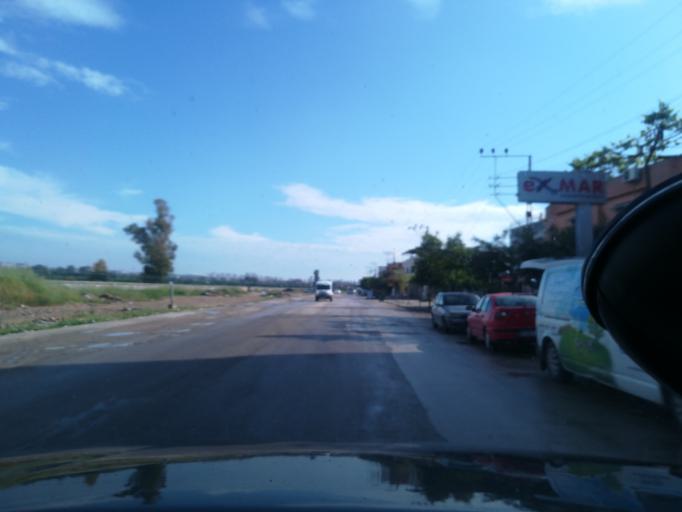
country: TR
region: Adana
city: Adana
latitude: 37.0127
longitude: 35.3596
